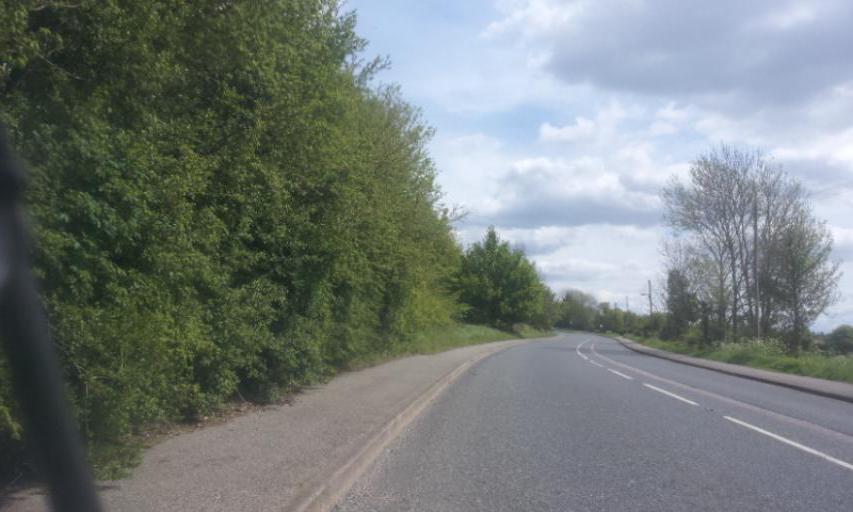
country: GB
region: England
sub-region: Kent
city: Longfield
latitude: 51.3914
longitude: 0.3273
